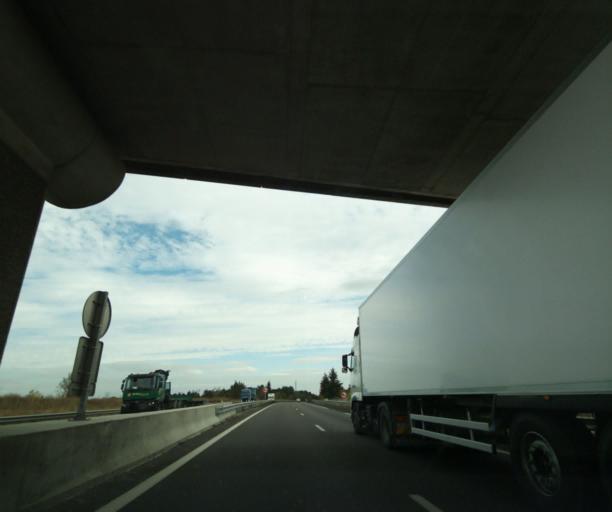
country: FR
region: Languedoc-Roussillon
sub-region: Departement du Gard
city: Garons
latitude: 43.7410
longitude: 4.4528
